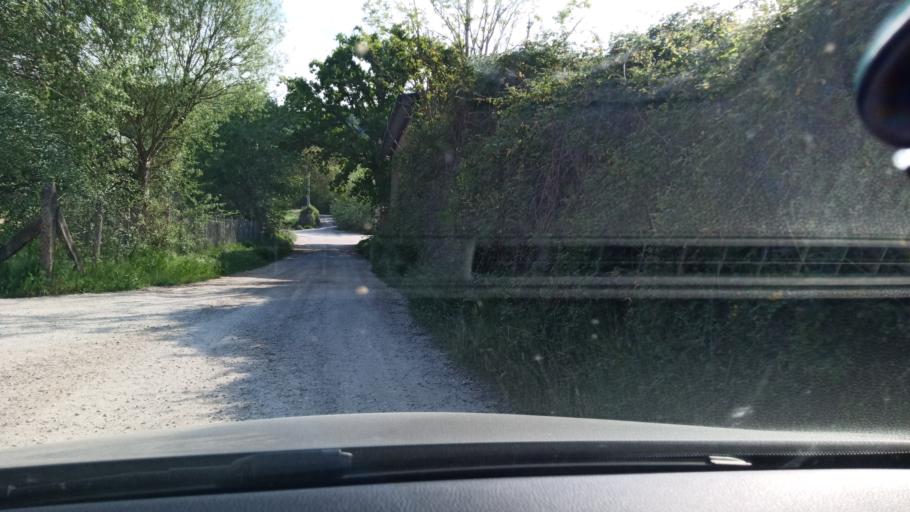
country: IT
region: Latium
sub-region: Citta metropolitana di Roma Capitale
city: Ponzano Romano
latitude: 42.2677
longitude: 12.5640
